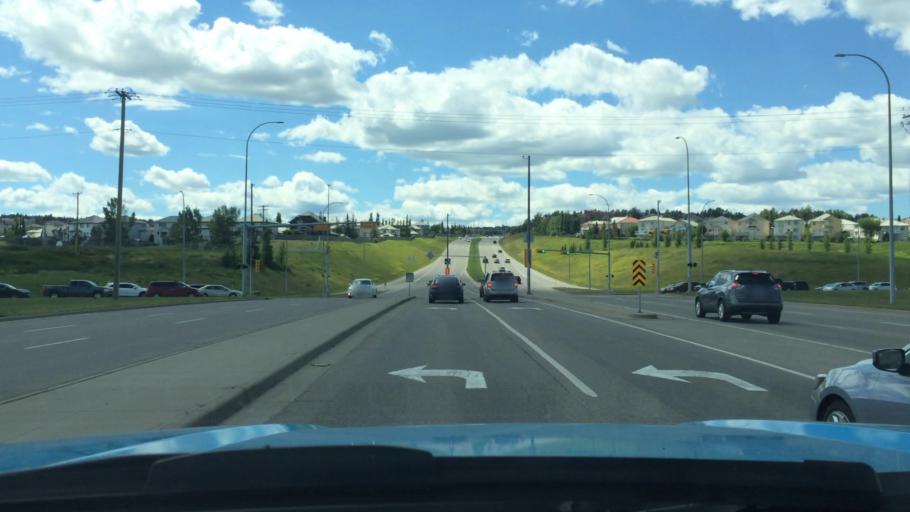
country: CA
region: Alberta
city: Calgary
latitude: 51.1430
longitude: -114.1220
